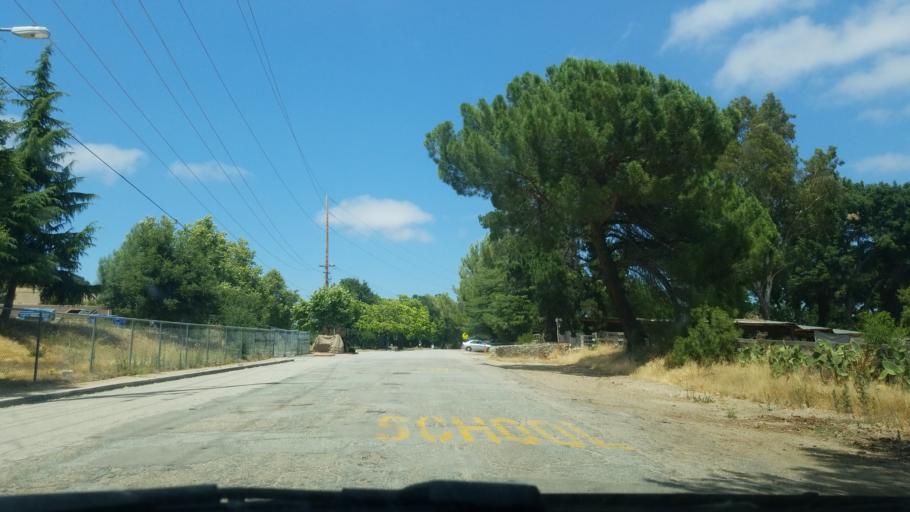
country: US
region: California
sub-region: San Luis Obispo County
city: Templeton
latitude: 35.5408
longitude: -120.7107
